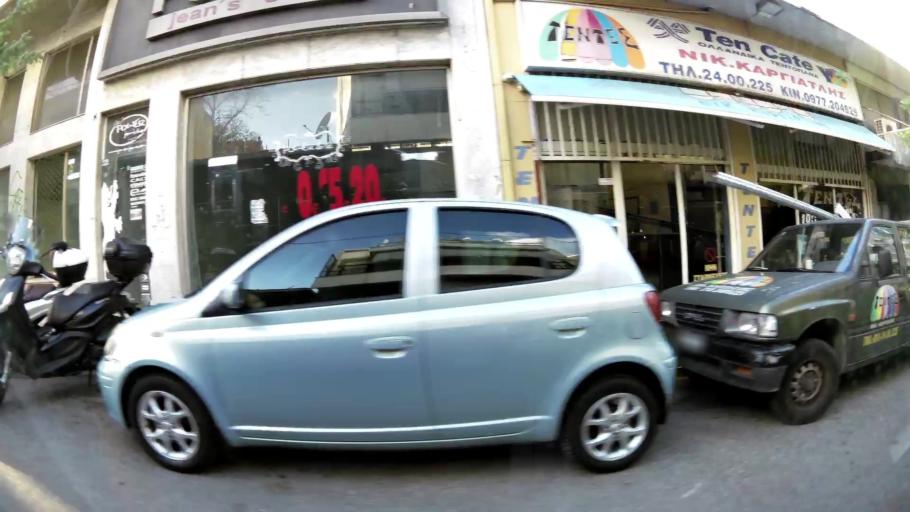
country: GR
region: Attica
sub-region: Nomarchia Anatolikis Attikis
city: Acharnes
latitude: 38.0793
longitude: 23.7371
